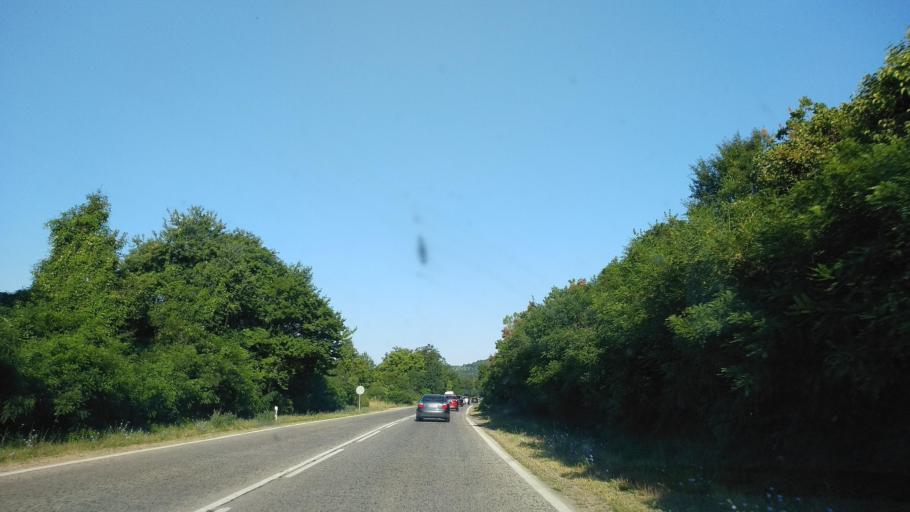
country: BG
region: Lovech
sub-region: Obshtina Lovech
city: Lovech
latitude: 43.0460
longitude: 24.8791
